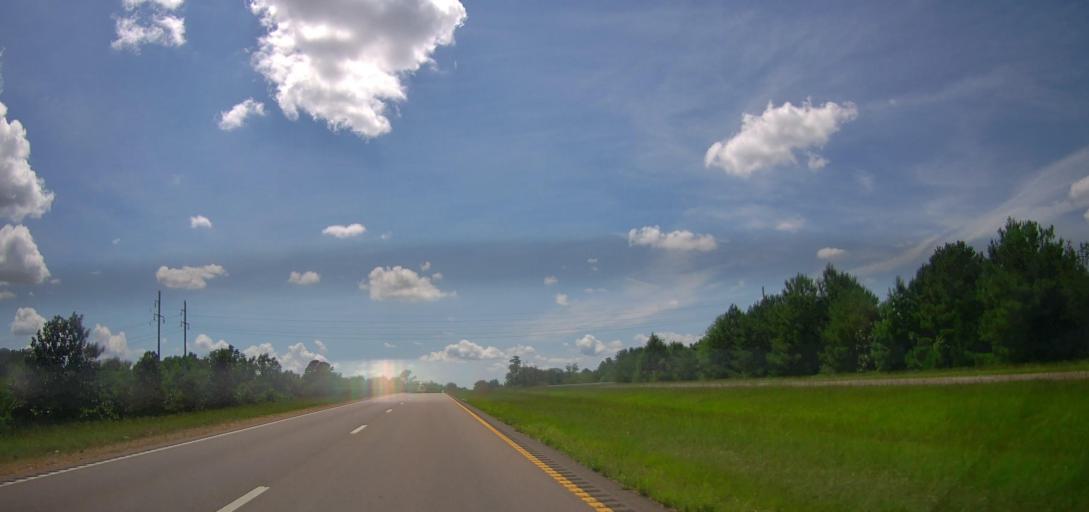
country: US
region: Mississippi
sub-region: Monroe County
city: Aberdeen
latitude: 33.8156
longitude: -88.5359
